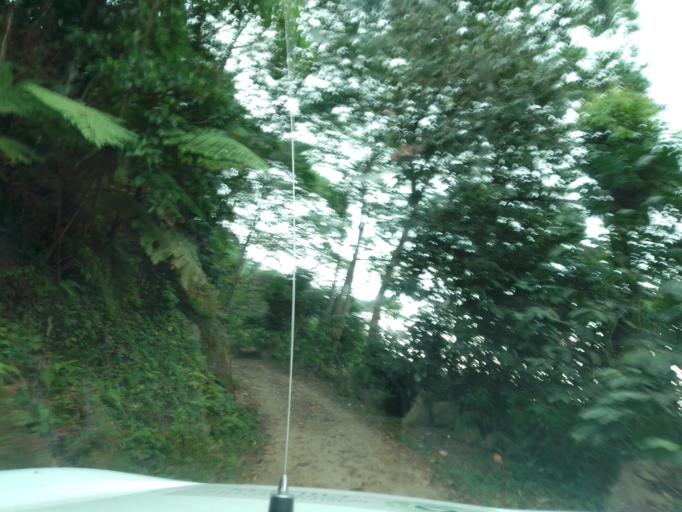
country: MX
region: Chiapas
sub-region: Union Juarez
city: Santo Domingo
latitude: 15.0652
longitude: -92.1244
